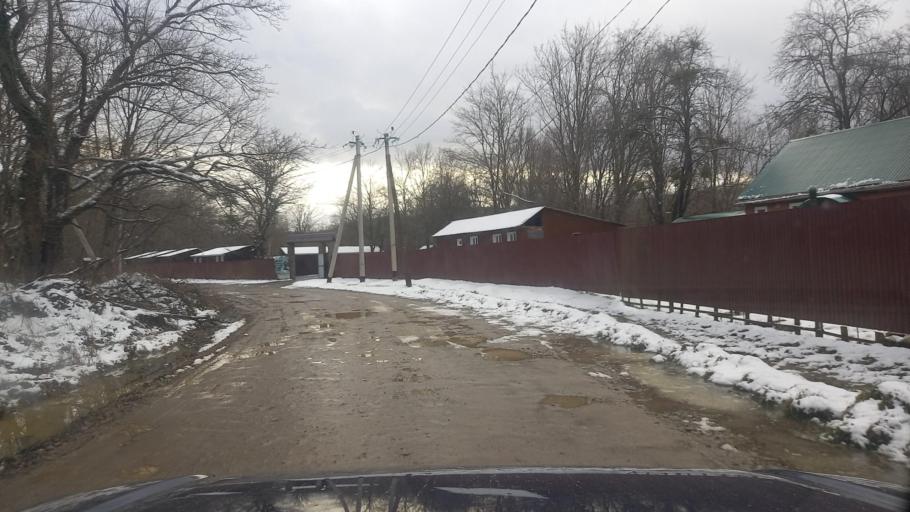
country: RU
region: Krasnodarskiy
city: Smolenskaya
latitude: 44.7025
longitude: 38.8261
